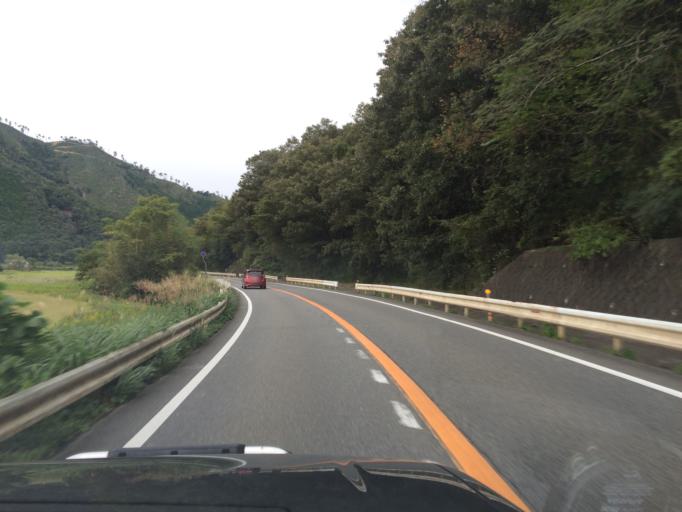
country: JP
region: Hyogo
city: Toyooka
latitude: 35.3714
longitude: 134.8170
